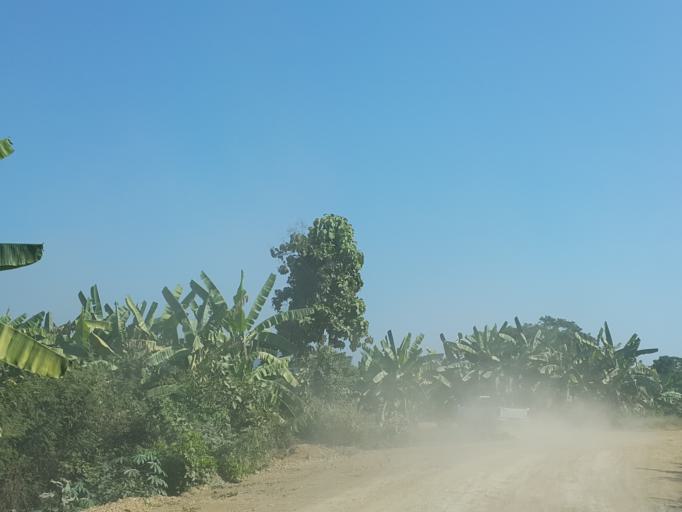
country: TH
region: Sukhothai
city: Thung Saliam
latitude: 17.3141
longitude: 99.4391
